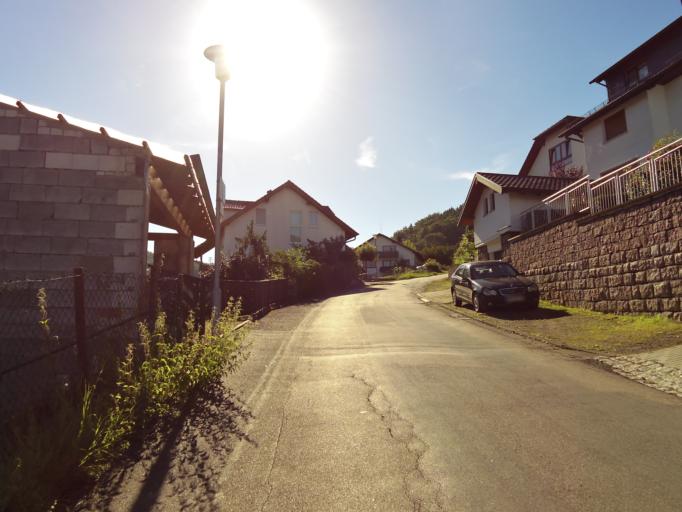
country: DE
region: Hesse
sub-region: Regierungsbezirk Darmstadt
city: Morlenbach
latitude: 49.5873
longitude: 8.7600
